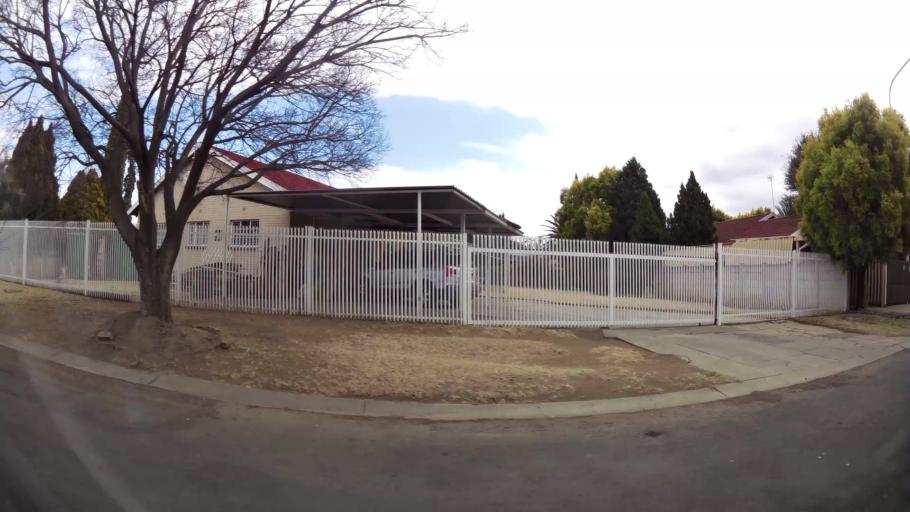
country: ZA
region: Orange Free State
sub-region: Fezile Dabi District Municipality
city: Kroonstad
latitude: -27.6332
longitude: 27.2422
